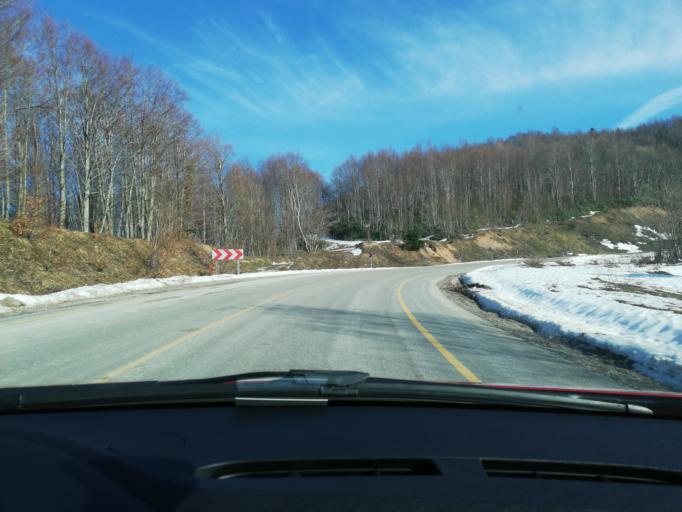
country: TR
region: Kastamonu
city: Cide
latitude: 41.8530
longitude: 33.0671
